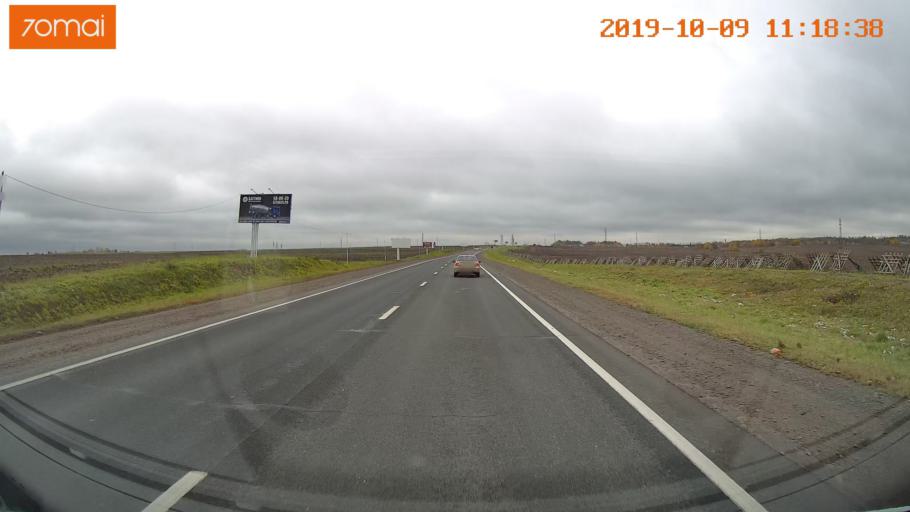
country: RU
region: Vologda
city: Vologda
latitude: 59.1661
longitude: 39.9173
